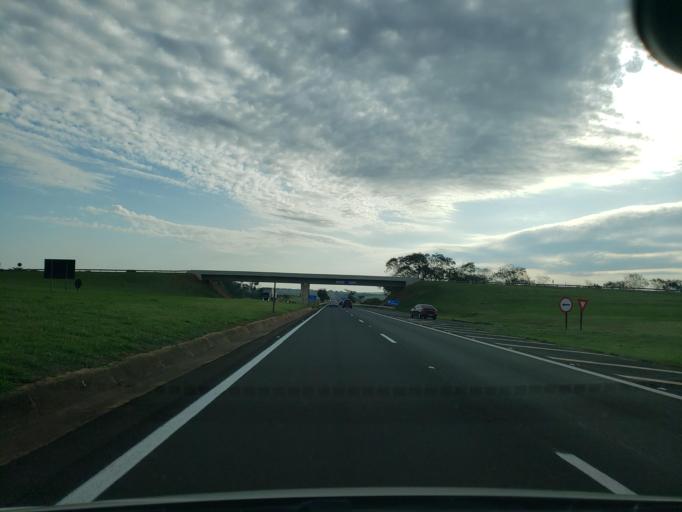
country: BR
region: Sao Paulo
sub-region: Guararapes
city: Guararapes
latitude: -21.2113
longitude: -50.7228
